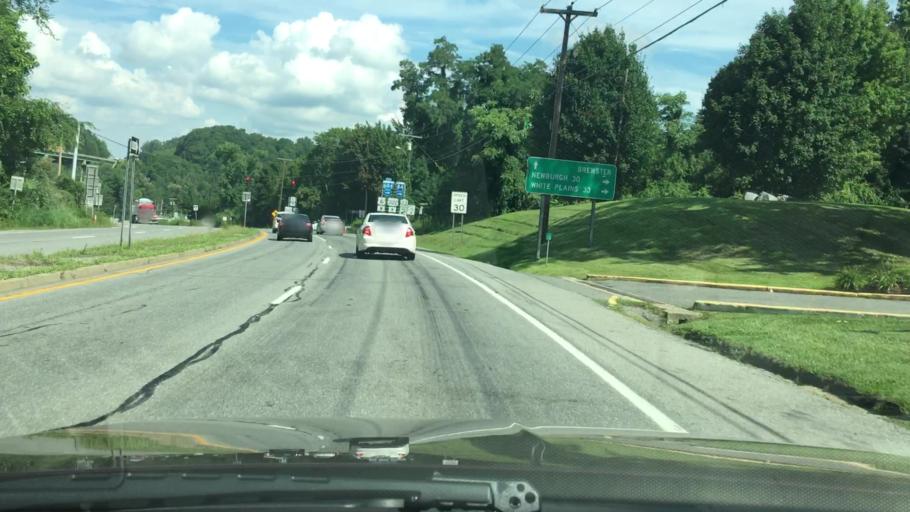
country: US
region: New York
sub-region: Putnam County
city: Brewster
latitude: 41.3960
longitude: -73.5969
